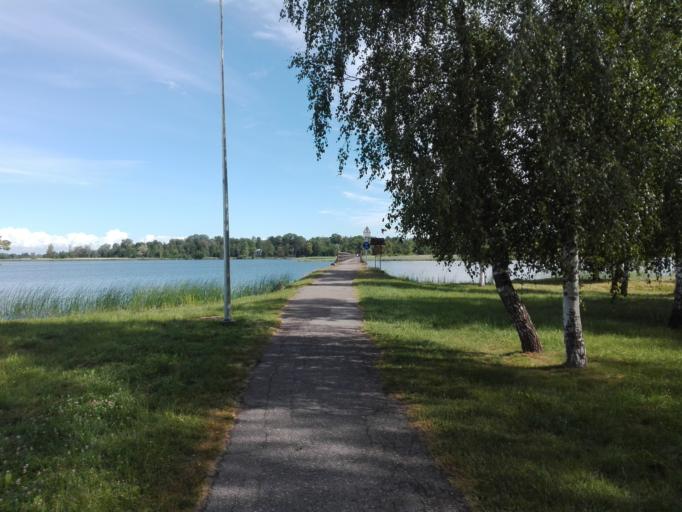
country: LT
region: Panevezys
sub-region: Birzai
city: Birzai
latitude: 56.2117
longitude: 24.7691
